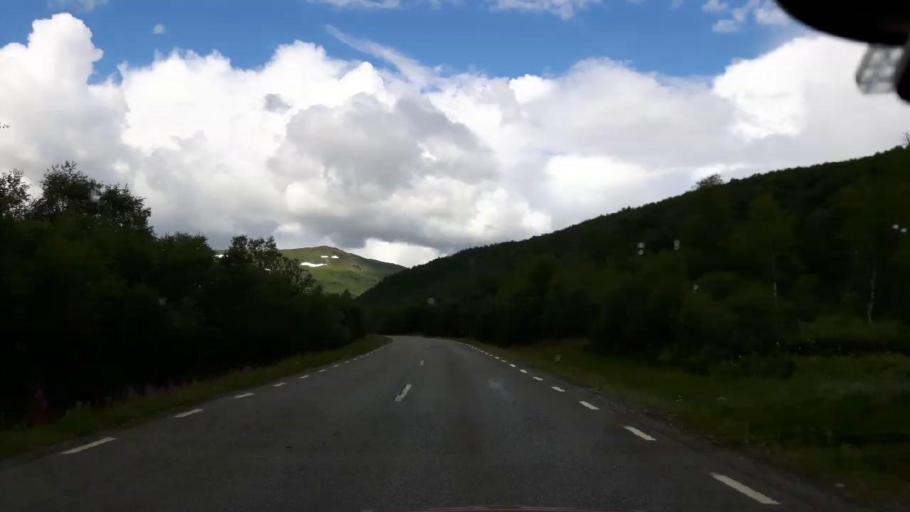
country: NO
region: Nordland
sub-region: Hattfjelldal
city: Hattfjelldal
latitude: 65.0673
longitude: 14.6835
